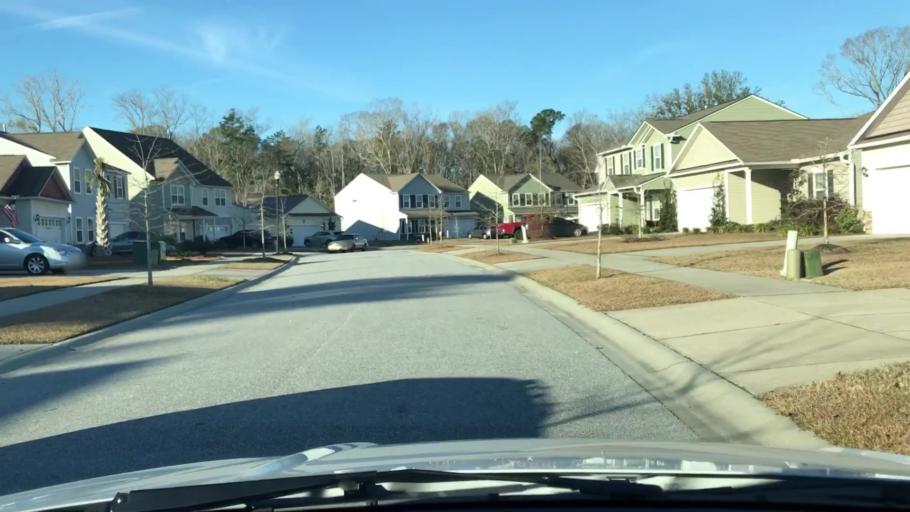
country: US
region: South Carolina
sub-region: Charleston County
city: Shell Point
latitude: 32.8124
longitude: -80.0742
